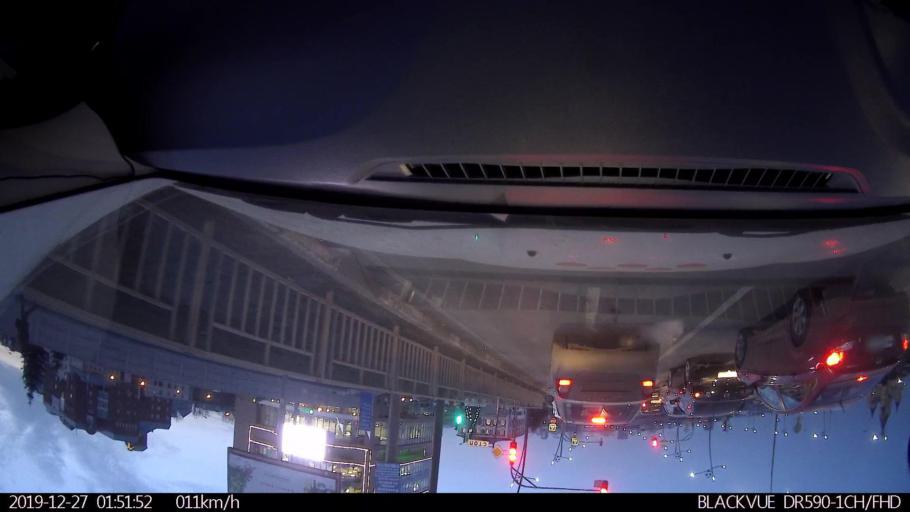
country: RU
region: Nizjnij Novgorod
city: Nizhniy Novgorod
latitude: 56.3336
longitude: 43.9624
